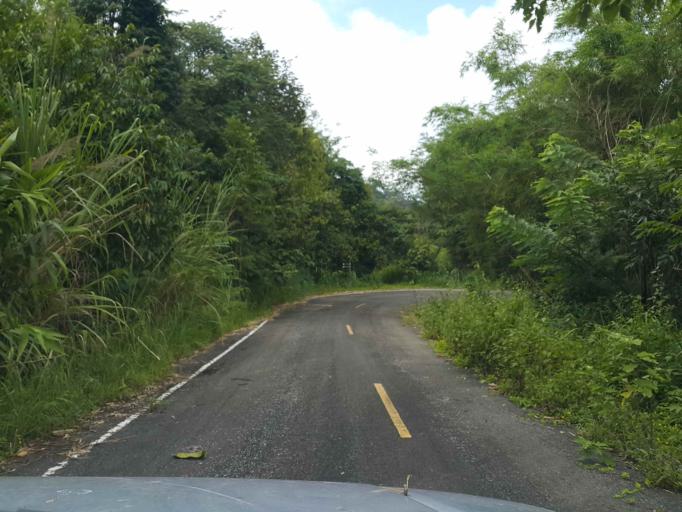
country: TH
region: Tak
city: Tak
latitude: 16.7932
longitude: 98.9236
